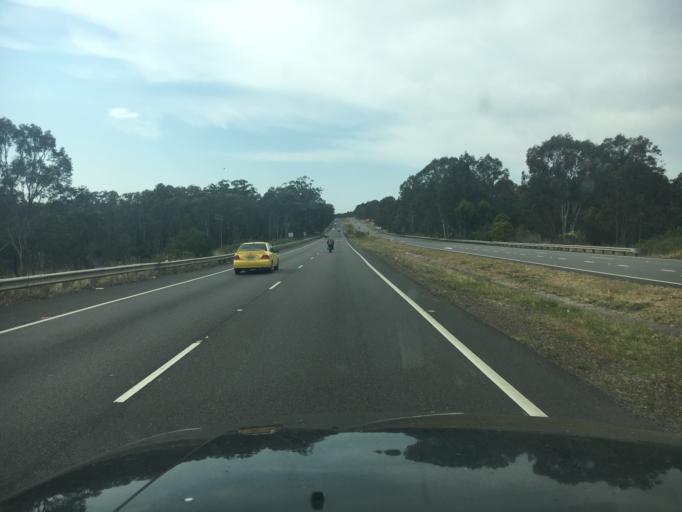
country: AU
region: New South Wales
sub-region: Maitland Municipality
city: East Maitland
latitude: -32.7760
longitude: 151.6129
